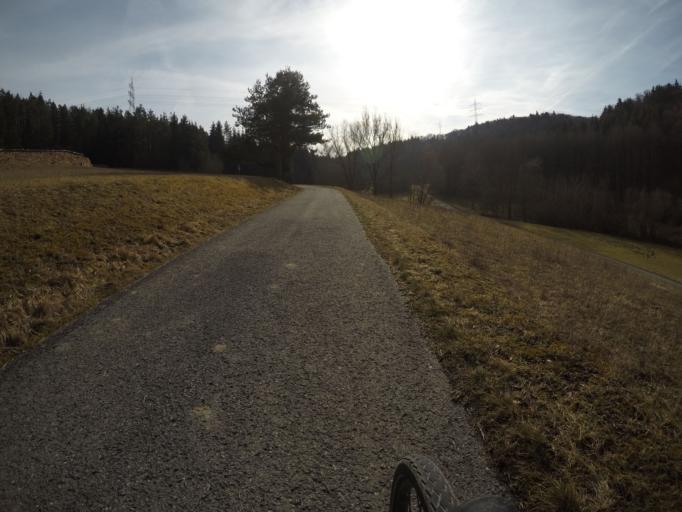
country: DE
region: Baden-Wuerttemberg
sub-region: Regierungsbezirk Stuttgart
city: Oberjettingen
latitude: 48.6091
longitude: 8.7851
